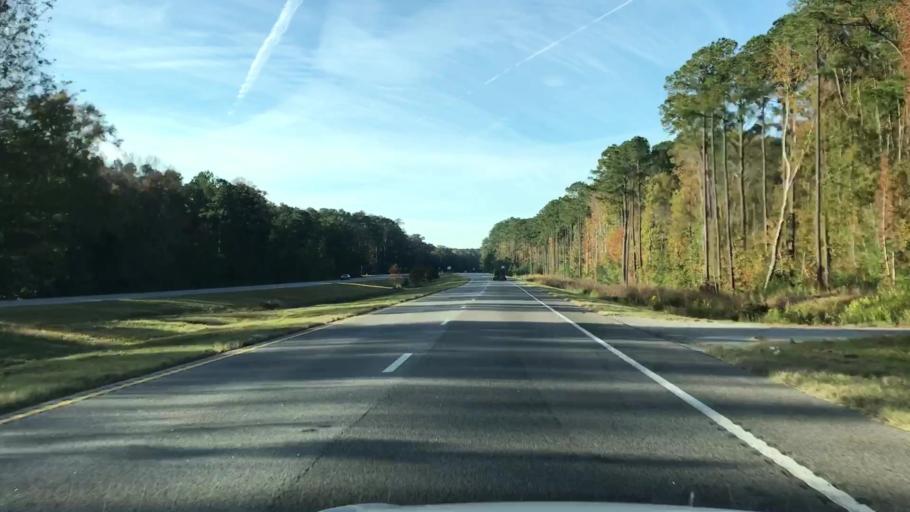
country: US
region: South Carolina
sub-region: Hampton County
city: Yemassee
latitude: 32.6703
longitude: -80.6485
